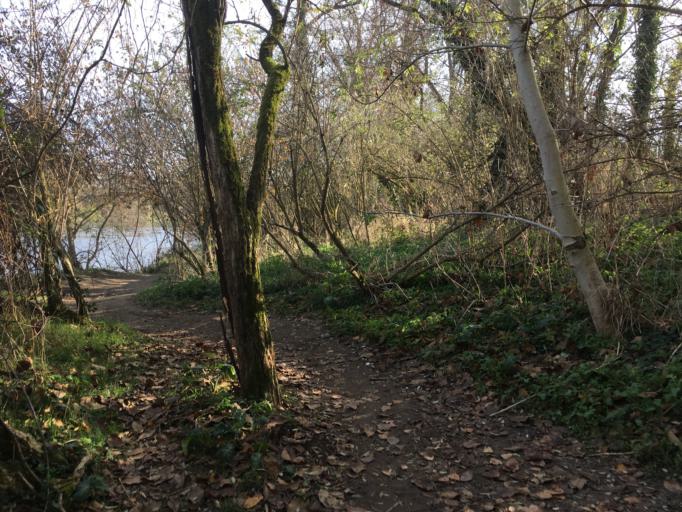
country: FR
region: Midi-Pyrenees
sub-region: Departement de la Haute-Garonne
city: Fenouillet
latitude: 43.6630
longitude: 1.4039
